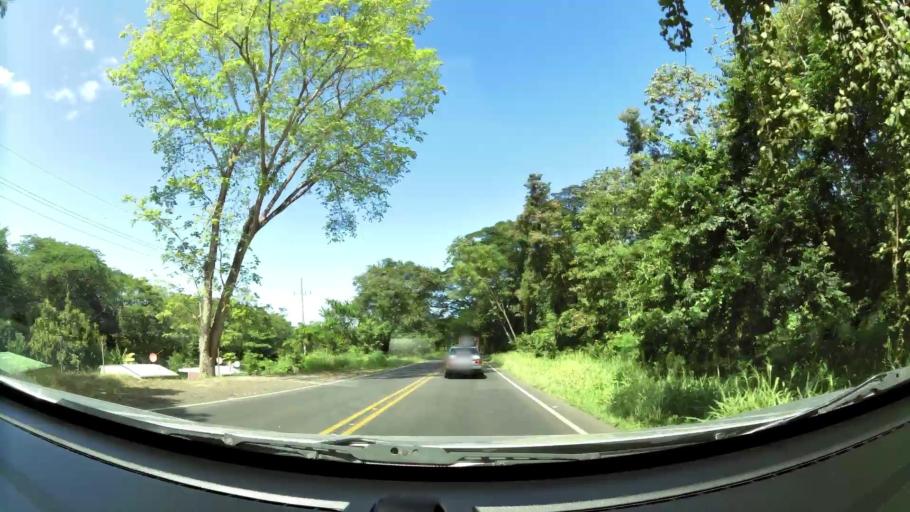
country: CR
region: Guanacaste
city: Juntas
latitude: 10.3105
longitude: -85.0409
